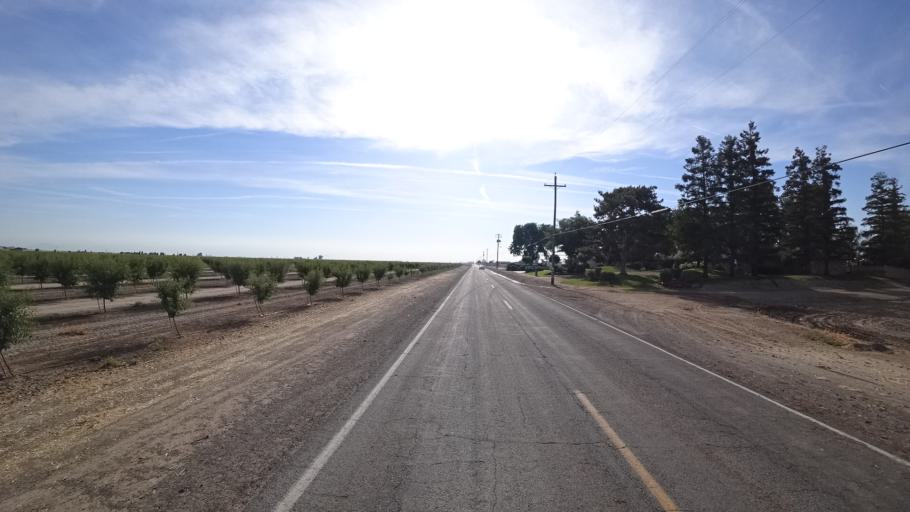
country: US
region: California
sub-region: Fresno County
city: Kingsburg
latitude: 36.4014
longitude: -119.5405
